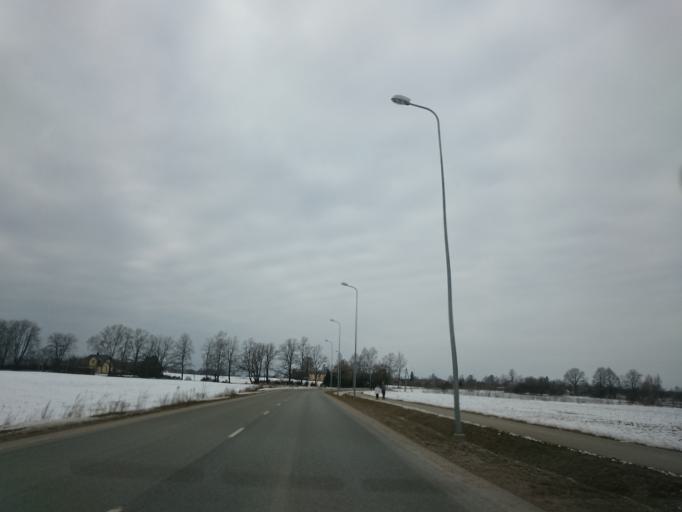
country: LV
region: Cesu Rajons
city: Cesis
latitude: 57.2967
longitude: 25.2521
